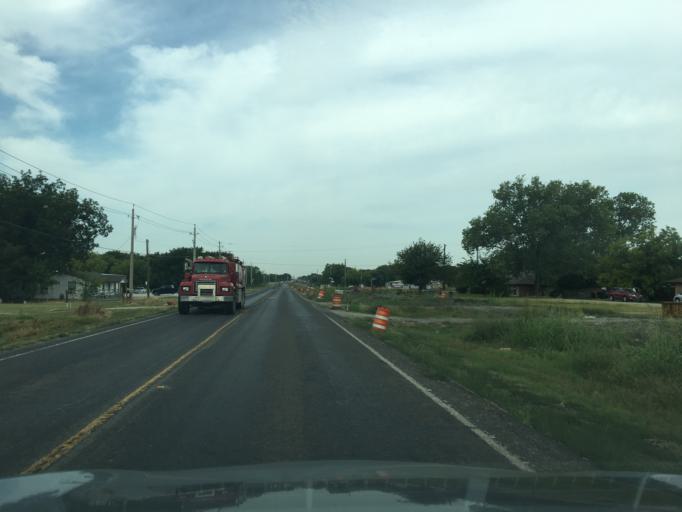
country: US
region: Texas
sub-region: Collin County
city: Lucas
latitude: 33.0550
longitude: -96.5841
